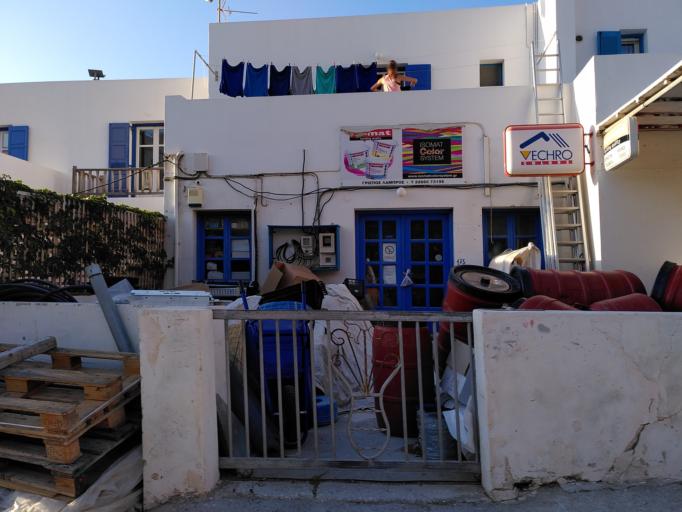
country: GR
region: South Aegean
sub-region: Nomos Kykladon
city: Amorgos
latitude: 36.9013
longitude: 25.9780
